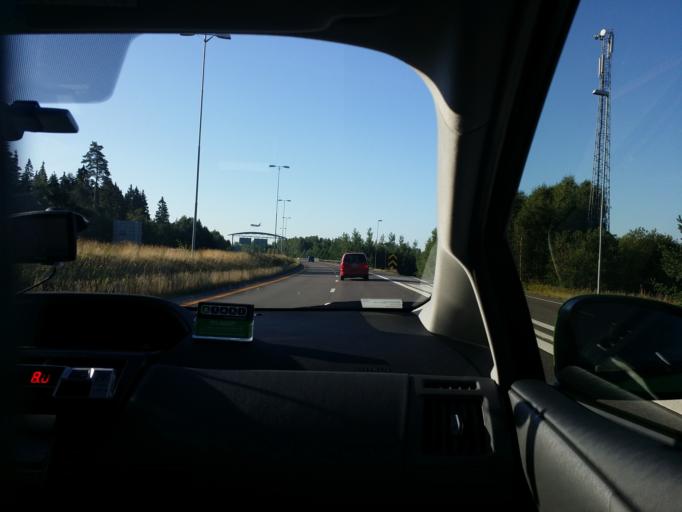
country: NO
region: Akershus
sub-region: Nannestad
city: Teigebyen
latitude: 60.1803
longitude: 11.0935
